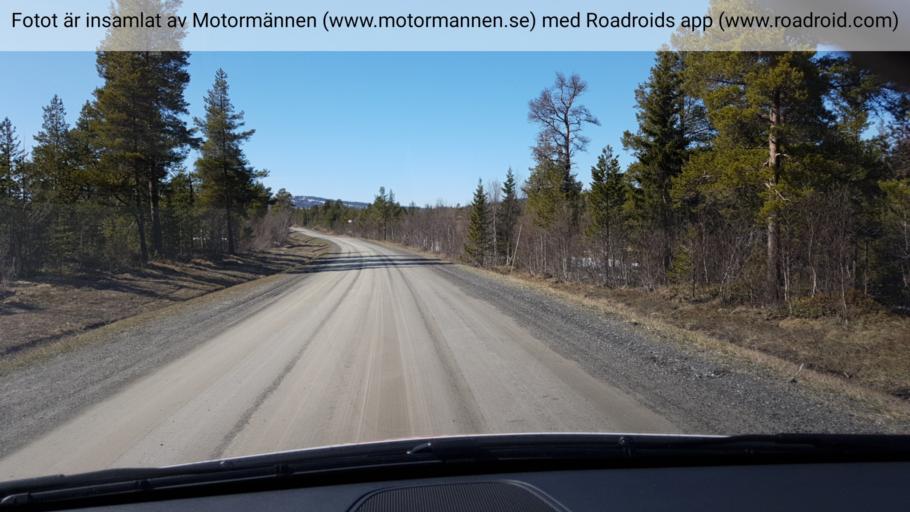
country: NO
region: Nord-Trondelag
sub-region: Snasa
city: Snaase
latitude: 63.7385
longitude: 12.4922
